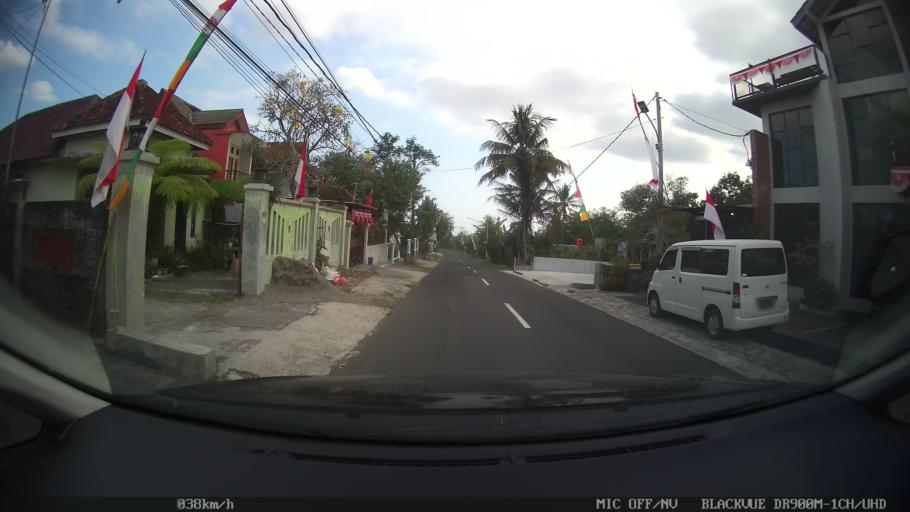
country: ID
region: Daerah Istimewa Yogyakarta
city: Melati
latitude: -7.6857
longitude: 110.4236
